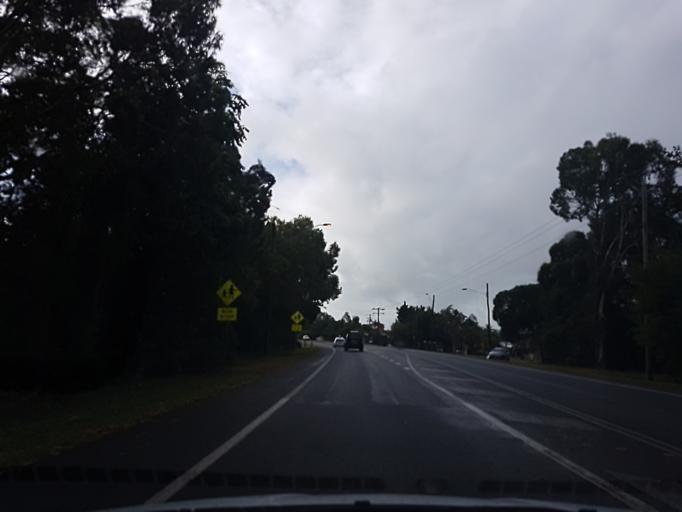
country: AU
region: Queensland
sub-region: Cairns
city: Trinity Beach
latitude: -16.7767
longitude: 145.6751
